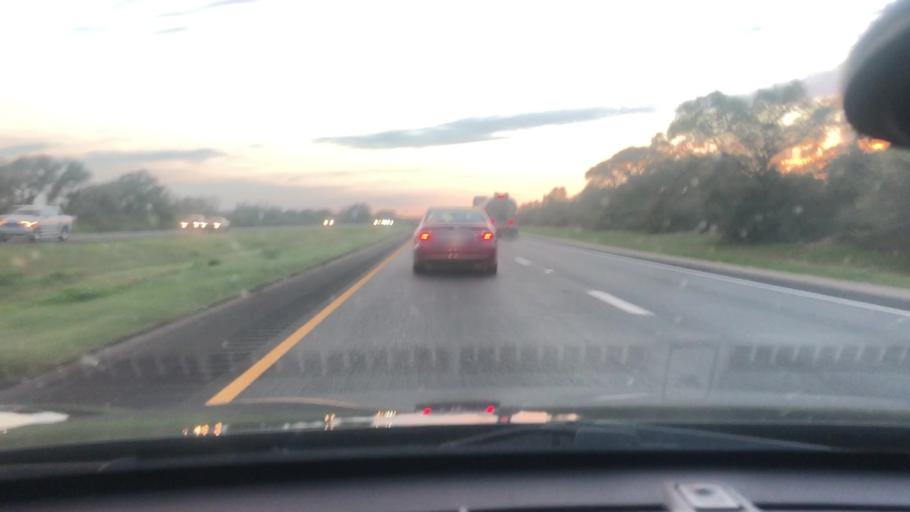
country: US
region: Texas
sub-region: Victoria County
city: Inez
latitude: 28.9173
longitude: -96.7663
